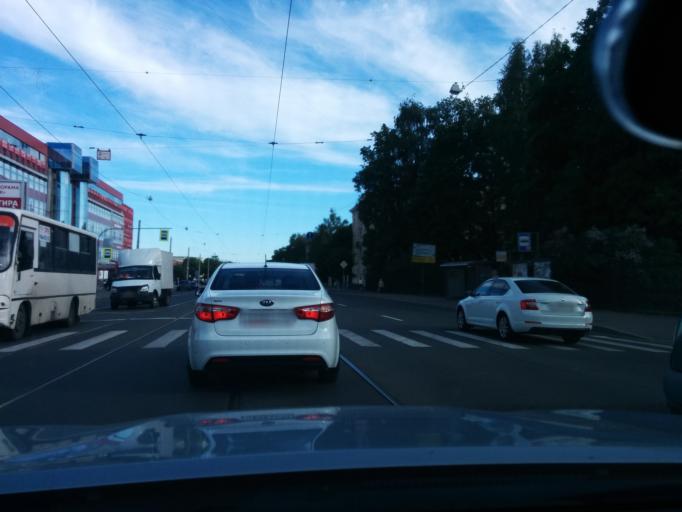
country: RU
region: Leningrad
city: Udel'naya
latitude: 60.0110
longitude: 30.3247
